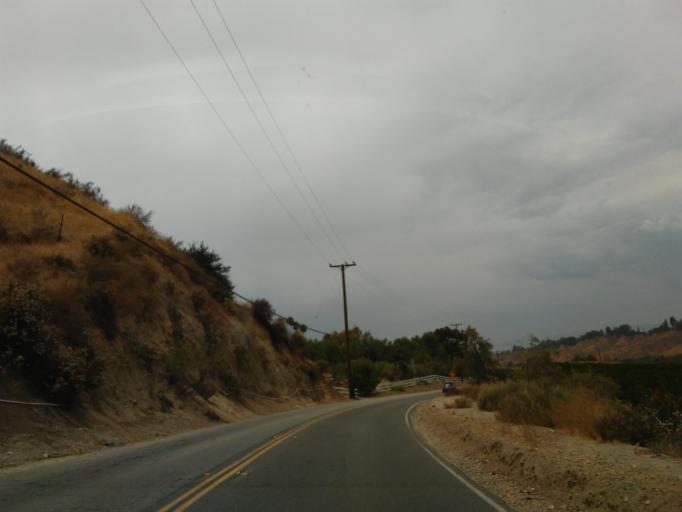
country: US
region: California
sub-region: San Bernardino County
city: Redlands
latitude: 34.0097
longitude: -117.1801
